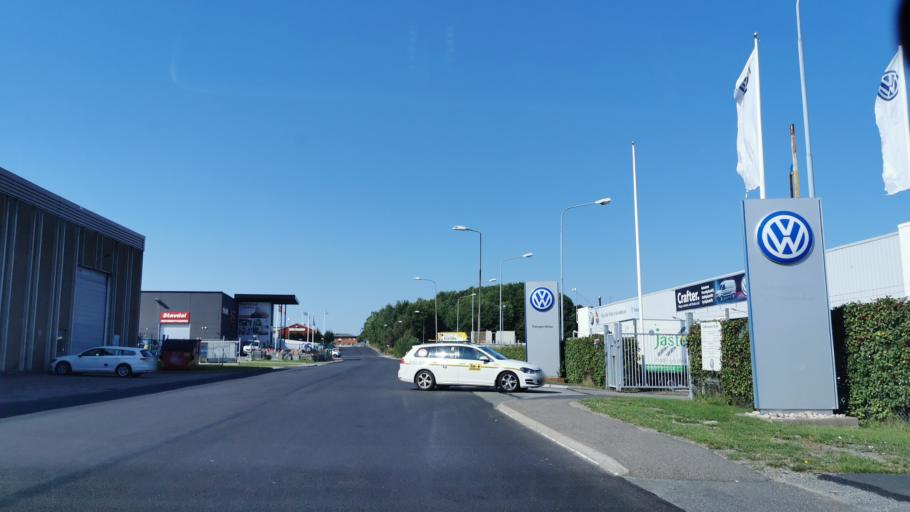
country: SE
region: Vaestra Goetaland
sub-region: Goteborg
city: Majorna
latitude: 57.6438
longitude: 11.9455
